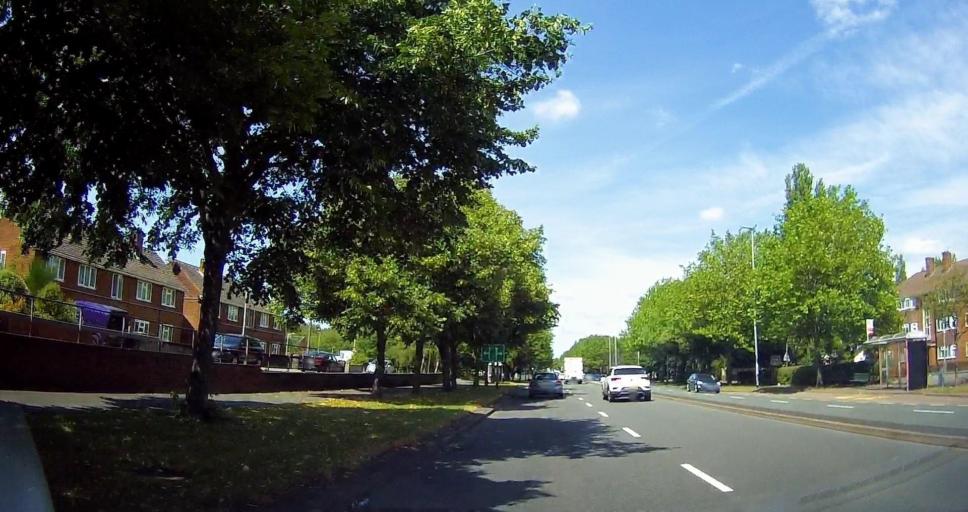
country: GB
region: England
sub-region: Wolverhampton
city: Wolverhampton
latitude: 52.5606
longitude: -2.1115
